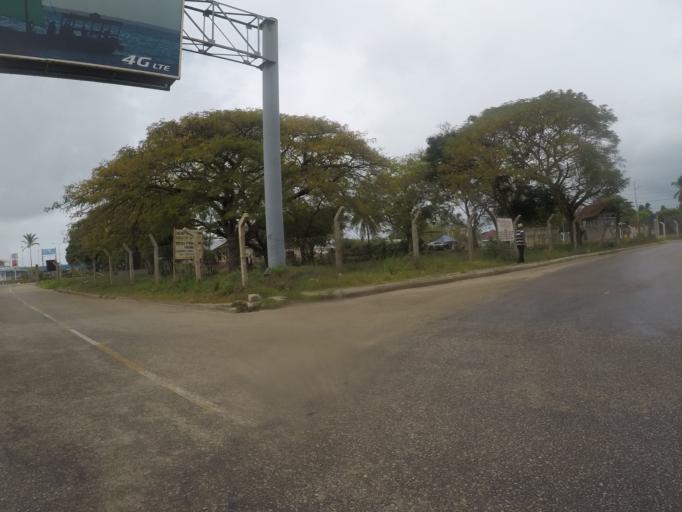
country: TZ
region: Zanzibar Urban/West
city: Zanzibar
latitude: -6.2164
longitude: 39.2205
